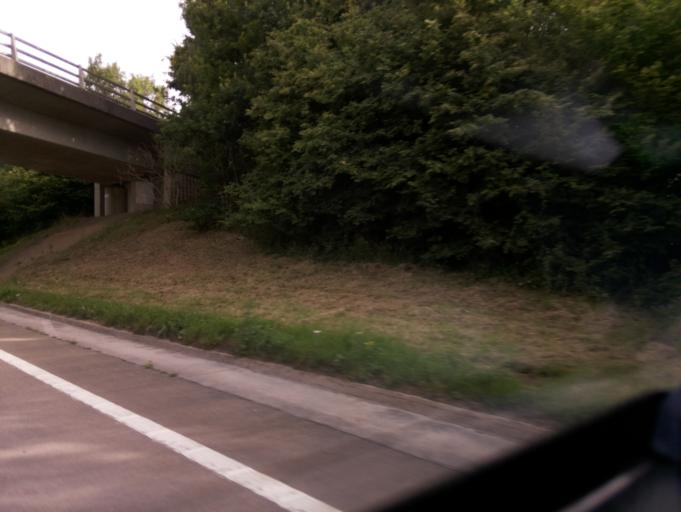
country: GB
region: England
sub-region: Wiltshire
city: Cricklade
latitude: 51.6642
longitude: -1.8854
